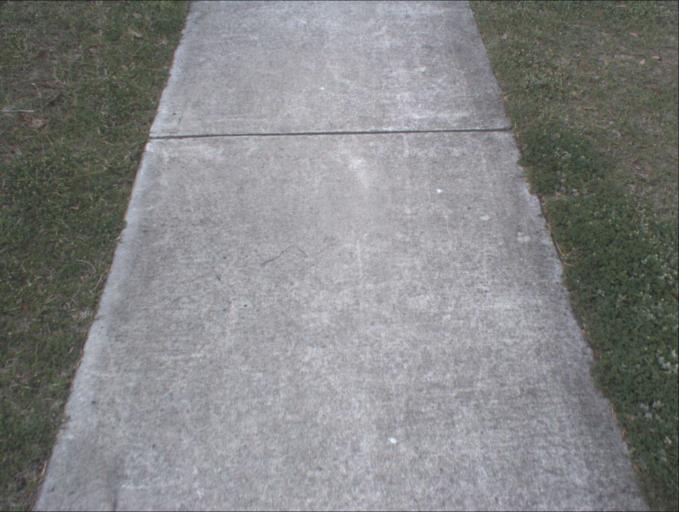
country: AU
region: Queensland
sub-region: Logan
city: Waterford West
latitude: -27.6873
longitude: 153.1177
